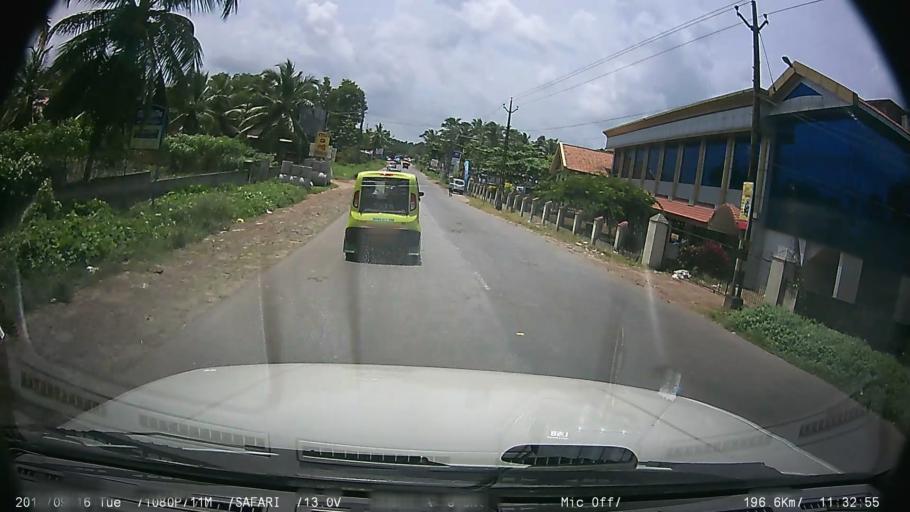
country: IN
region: Kerala
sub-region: Kottayam
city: Changanacheri
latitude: 9.4708
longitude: 76.5292
